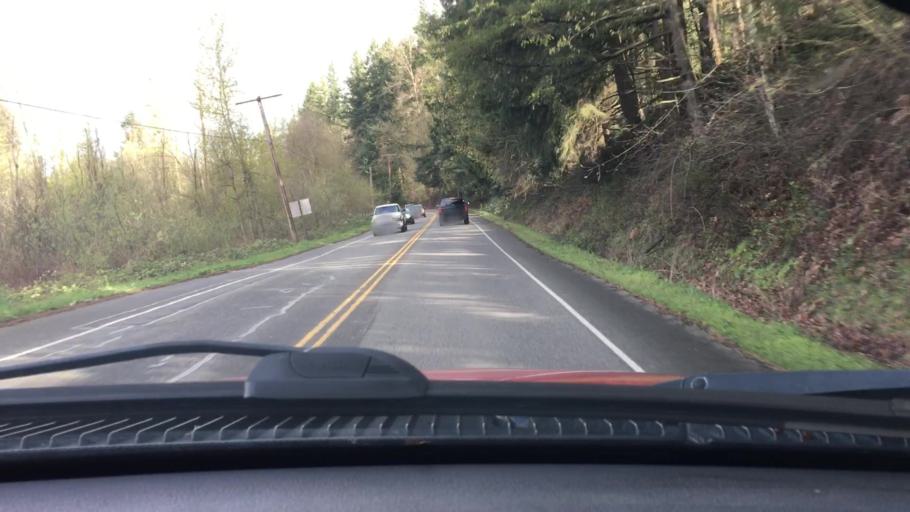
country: US
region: Washington
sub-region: King County
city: Maple Valley
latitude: 47.3678
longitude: -122.0436
